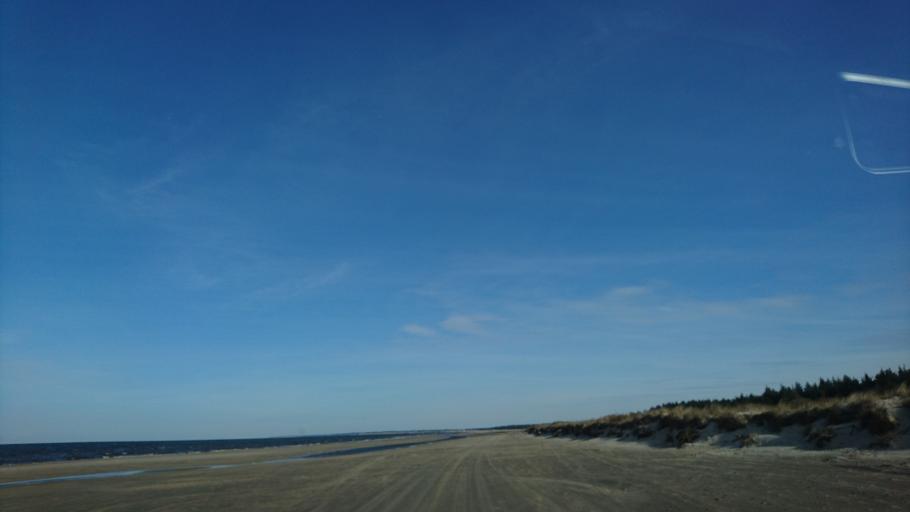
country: DK
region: North Denmark
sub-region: Hjorring Kommune
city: Hirtshals
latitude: 57.5910
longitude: 10.0520
